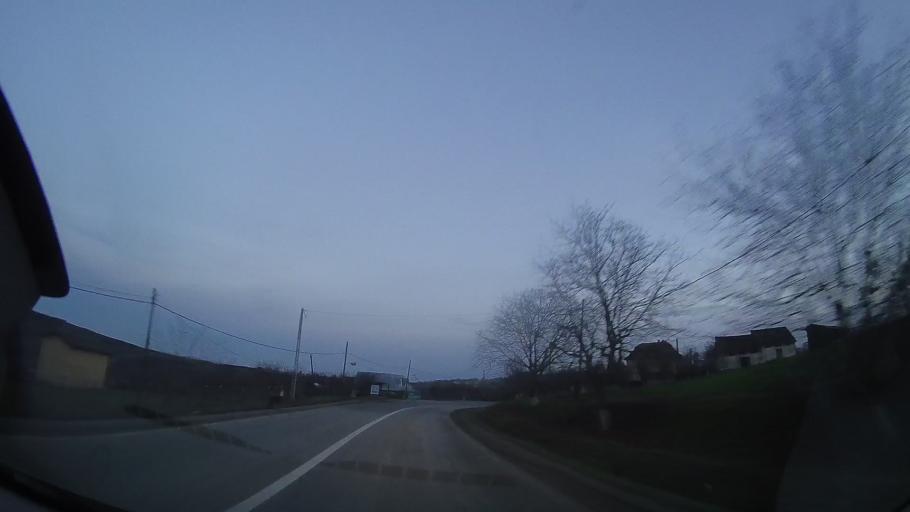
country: RO
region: Cluj
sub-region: Comuna Mociu
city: Mociu
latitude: 46.7925
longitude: 24.0696
